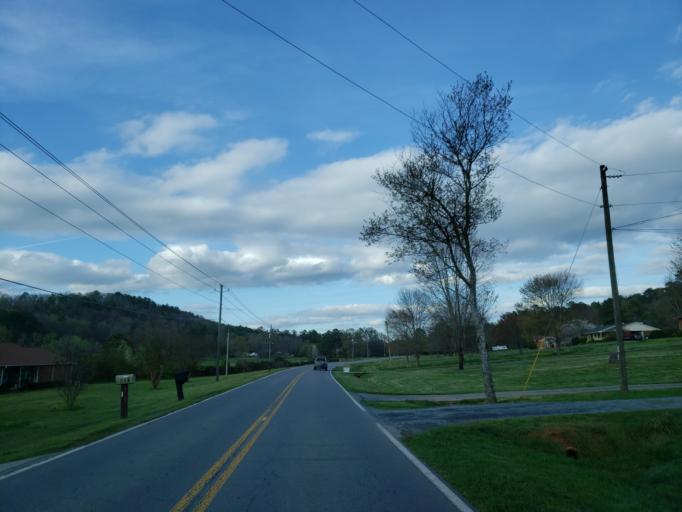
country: US
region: Georgia
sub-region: Bartow County
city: Cartersville
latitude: 34.2359
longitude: -84.8161
